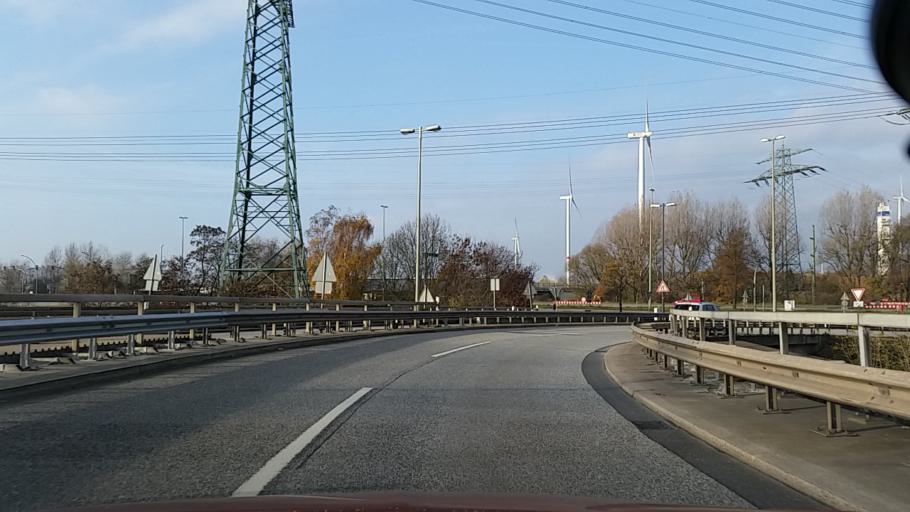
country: DE
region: Hamburg
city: Altona
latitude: 53.5140
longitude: 9.9146
